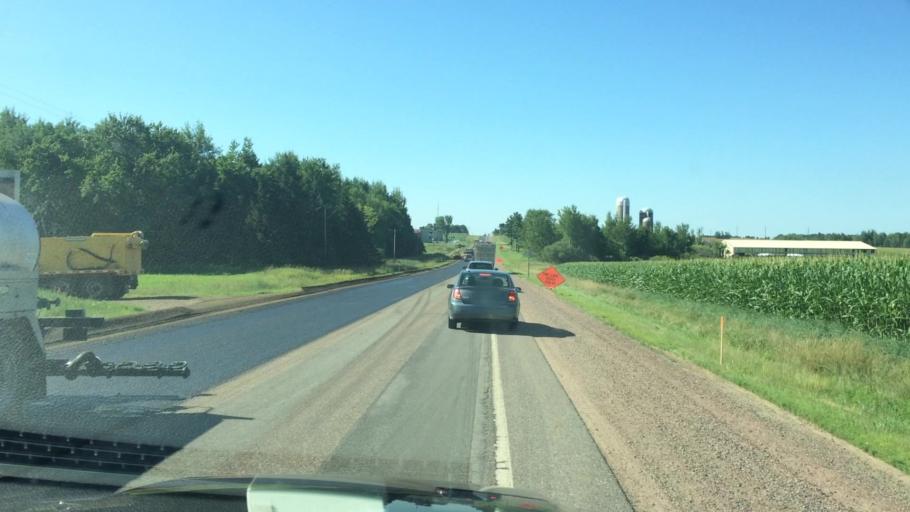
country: US
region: Wisconsin
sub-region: Marathon County
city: Stratford
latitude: 44.8975
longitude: -90.0788
